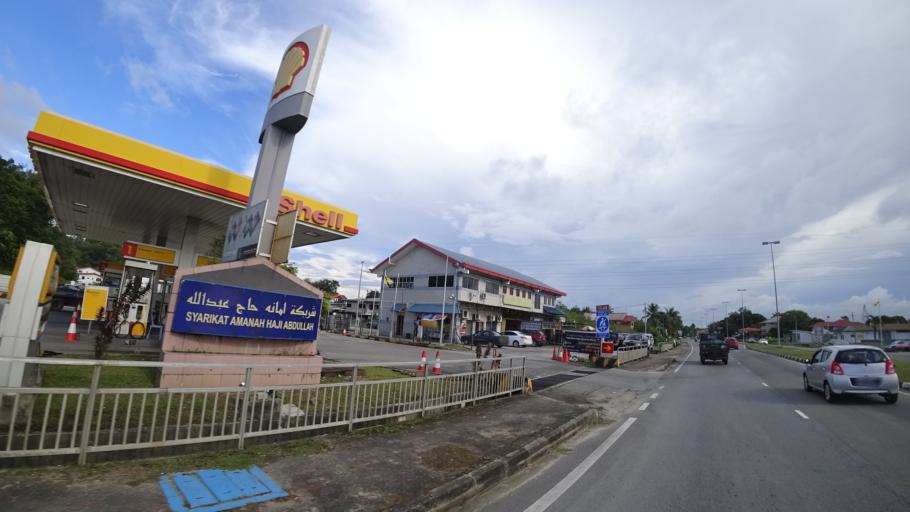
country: BN
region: Brunei and Muara
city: Bandar Seri Begawan
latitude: 4.8760
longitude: 114.8606
